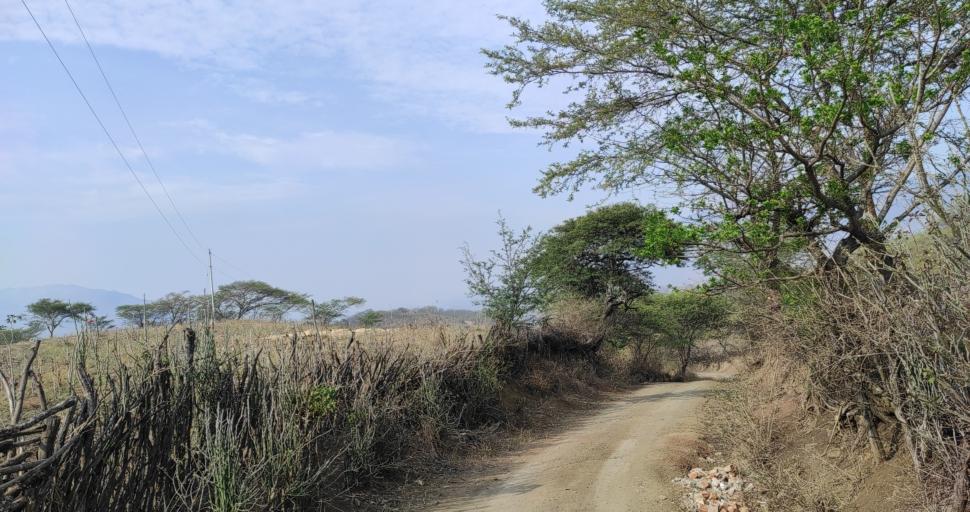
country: EC
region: Loja
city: Catacocha
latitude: -4.0086
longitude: -79.6985
